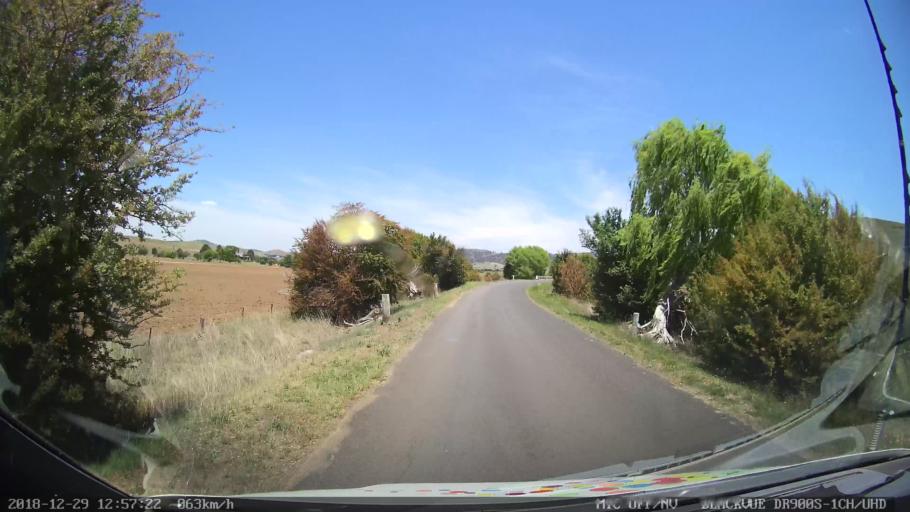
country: AU
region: Australian Capital Territory
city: Macarthur
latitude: -35.7077
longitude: 149.1779
